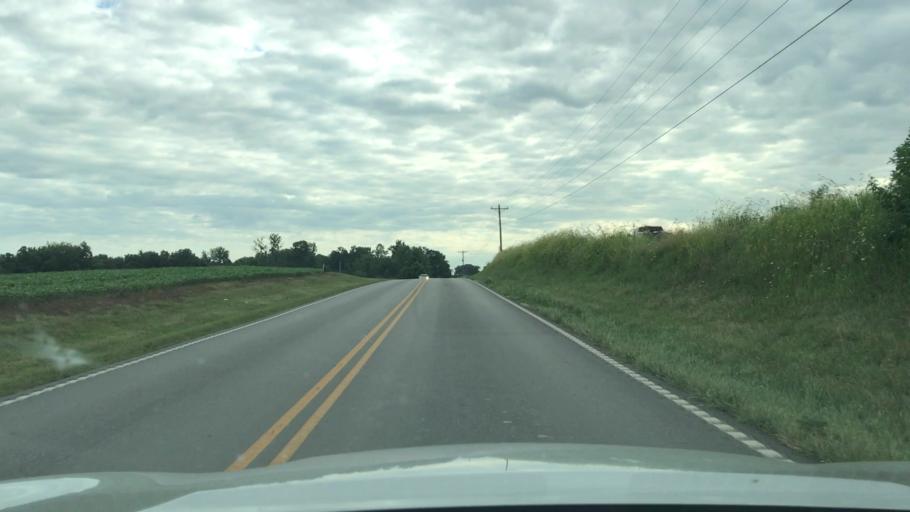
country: US
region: Kentucky
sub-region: Todd County
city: Elkton
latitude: 36.7461
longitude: -87.1761
